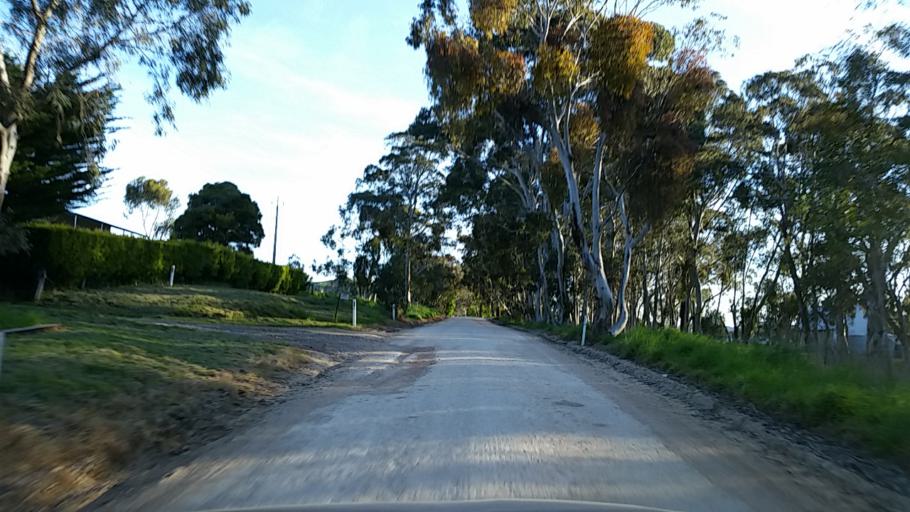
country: AU
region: South Australia
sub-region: Alexandrina
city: Mount Compass
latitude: -35.2796
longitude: 138.6997
